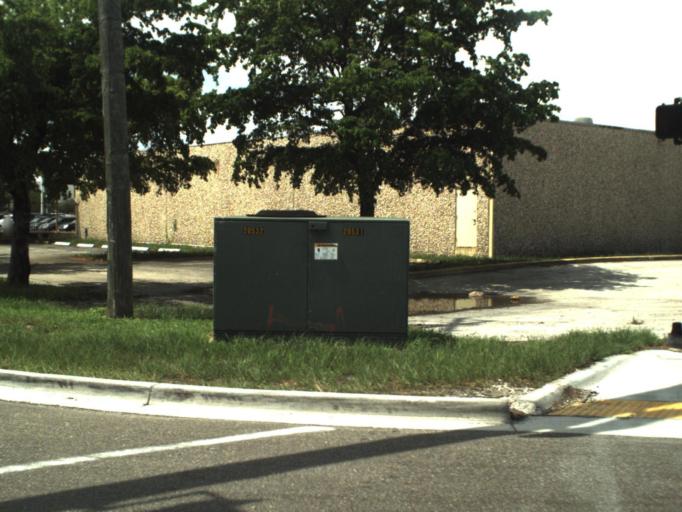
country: US
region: Florida
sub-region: Broward County
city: Dania Beach
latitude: 26.0820
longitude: -80.1244
